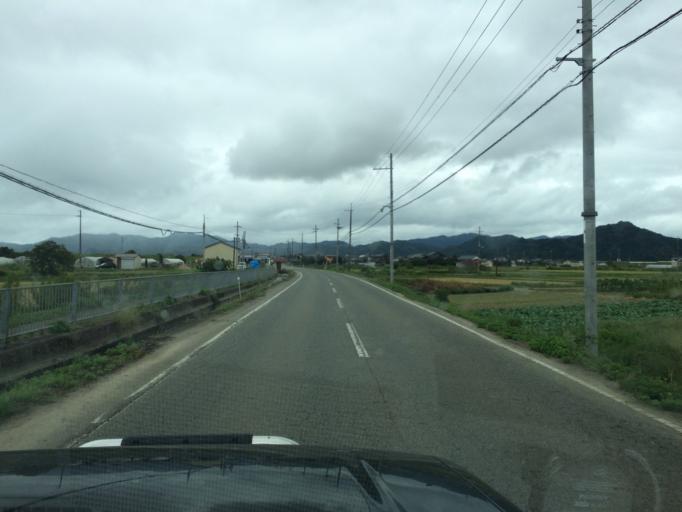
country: JP
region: Hyogo
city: Toyooka
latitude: 35.5054
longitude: 134.8225
